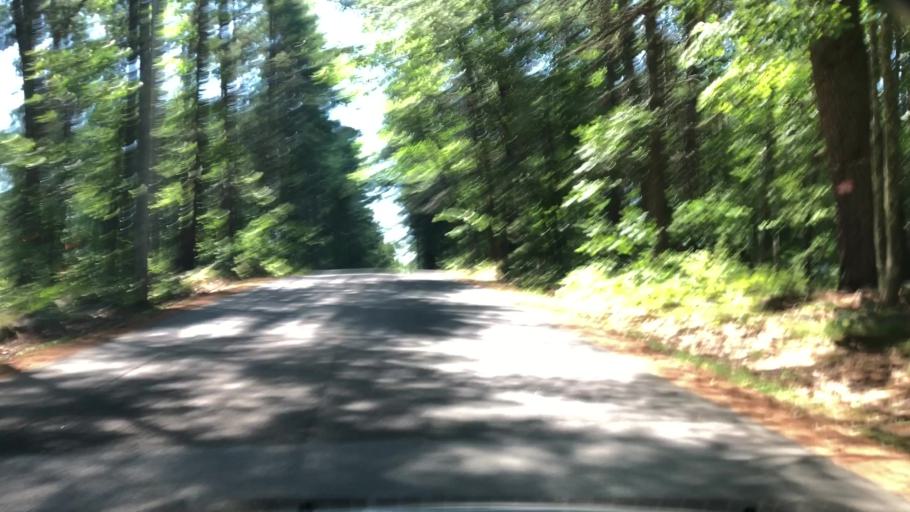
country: US
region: New Hampshire
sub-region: Hillsborough County
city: Milford
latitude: 42.8561
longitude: -71.5798
